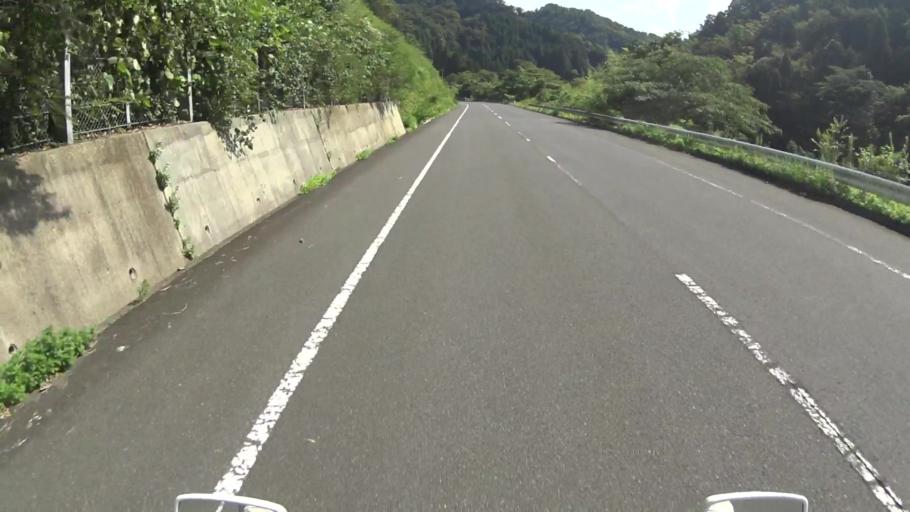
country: JP
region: Kyoto
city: Miyazu
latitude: 35.6352
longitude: 135.2038
